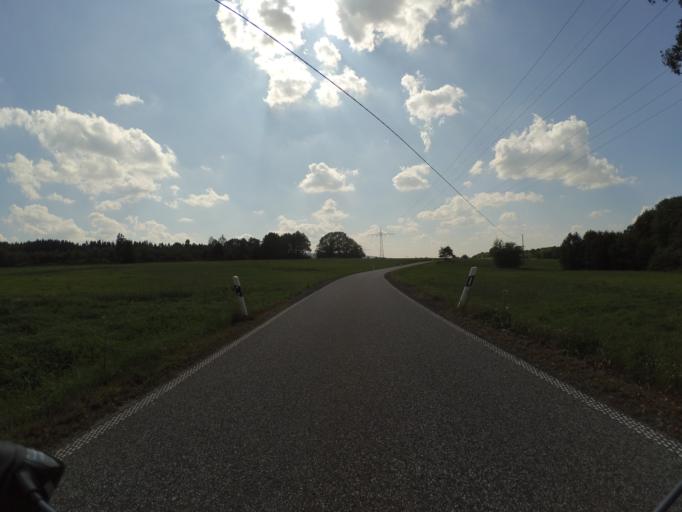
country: DE
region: Rheinland-Pfalz
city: Kommen
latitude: 49.8403
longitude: 7.1720
